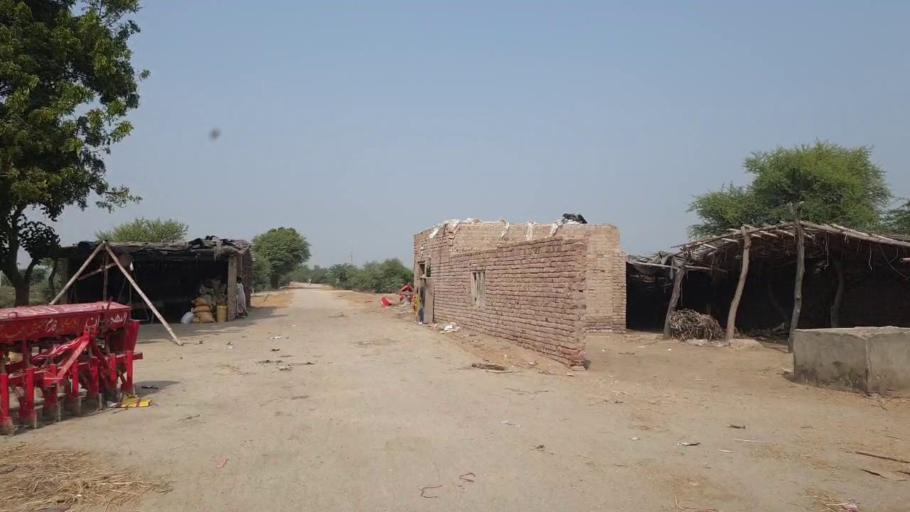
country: PK
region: Sindh
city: Kario
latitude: 24.9168
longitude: 68.6019
